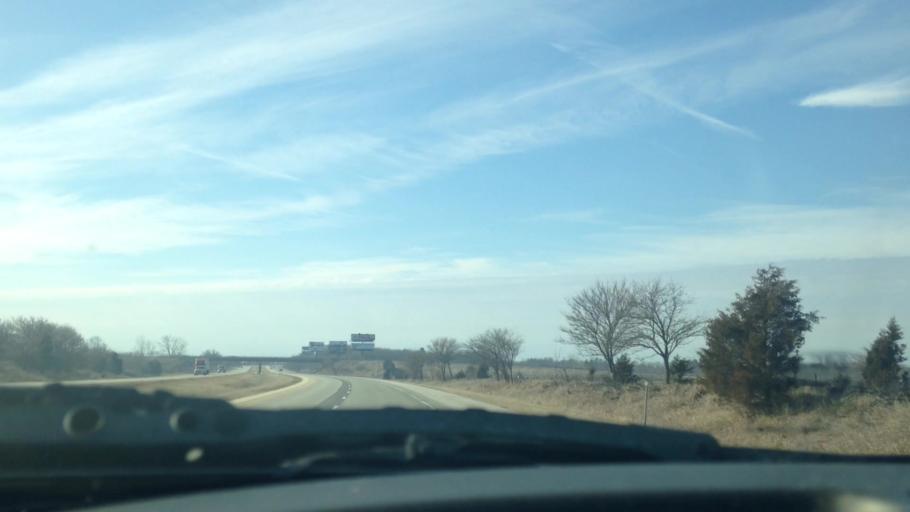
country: US
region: Illinois
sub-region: Ford County
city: Paxton
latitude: 40.5213
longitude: -88.0846
